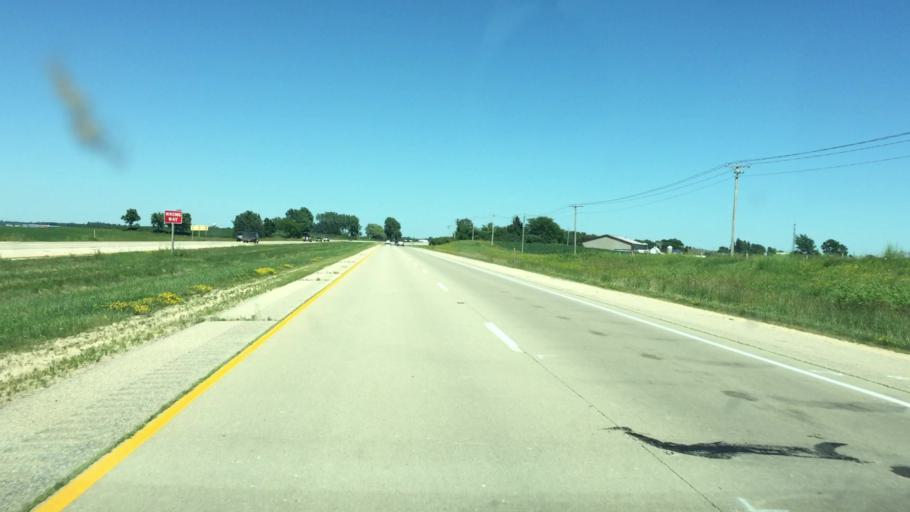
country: US
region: Wisconsin
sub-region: Iowa County
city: Mineral Point
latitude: 42.8363
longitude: -90.2248
